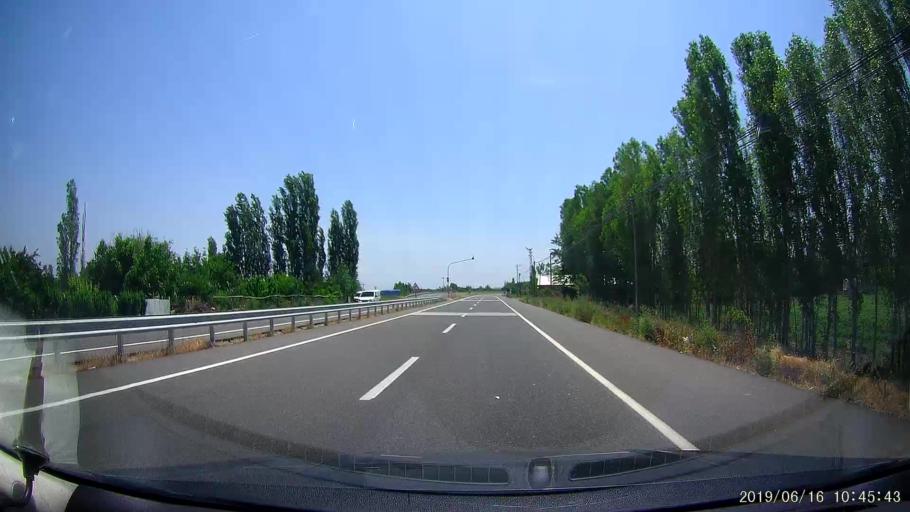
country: AM
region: Armavir
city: Shenavan
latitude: 40.0267
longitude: 43.8724
